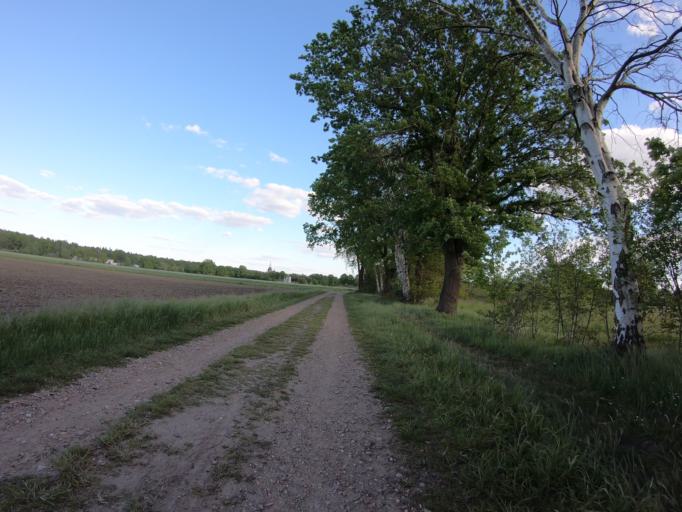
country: DE
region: Lower Saxony
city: Gifhorn
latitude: 52.4973
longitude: 10.5505
